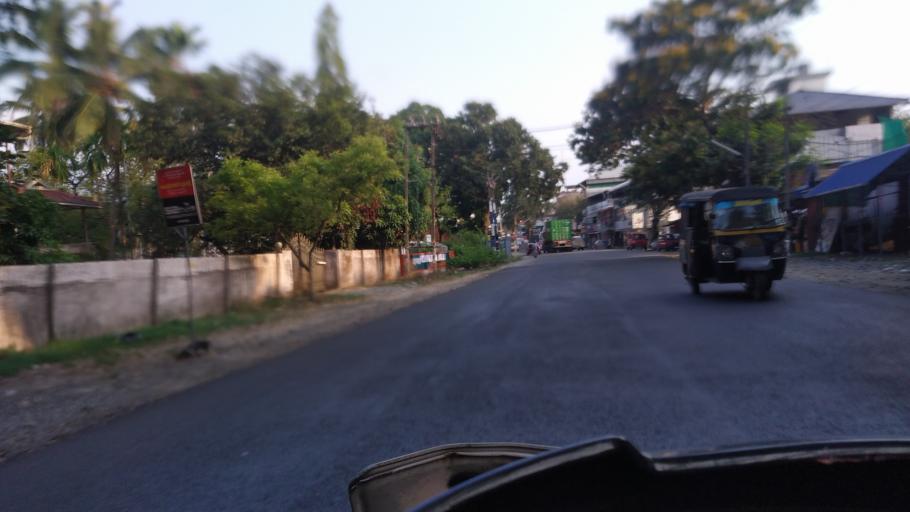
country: IN
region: Kerala
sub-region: Thrissur District
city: Thanniyam
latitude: 10.3580
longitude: 76.1273
